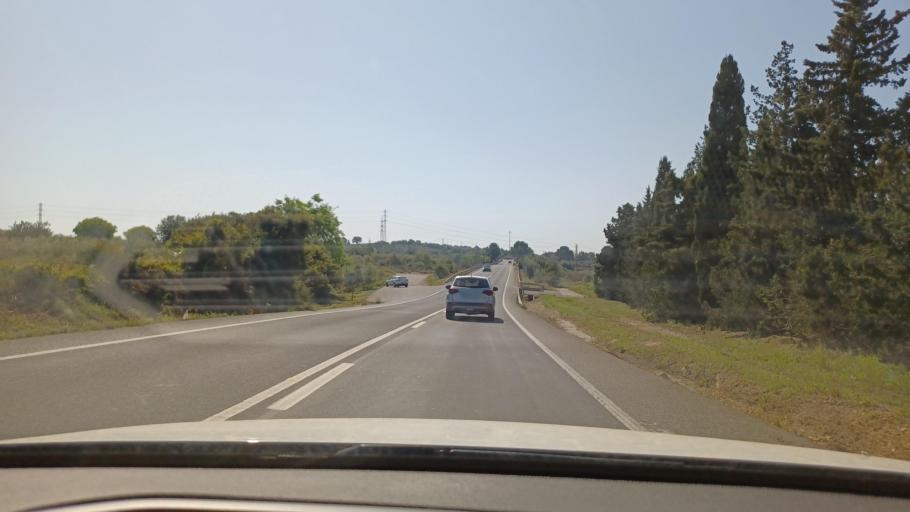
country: ES
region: Catalonia
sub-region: Provincia de Tarragona
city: Masdenverge
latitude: 40.7078
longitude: 0.5457
